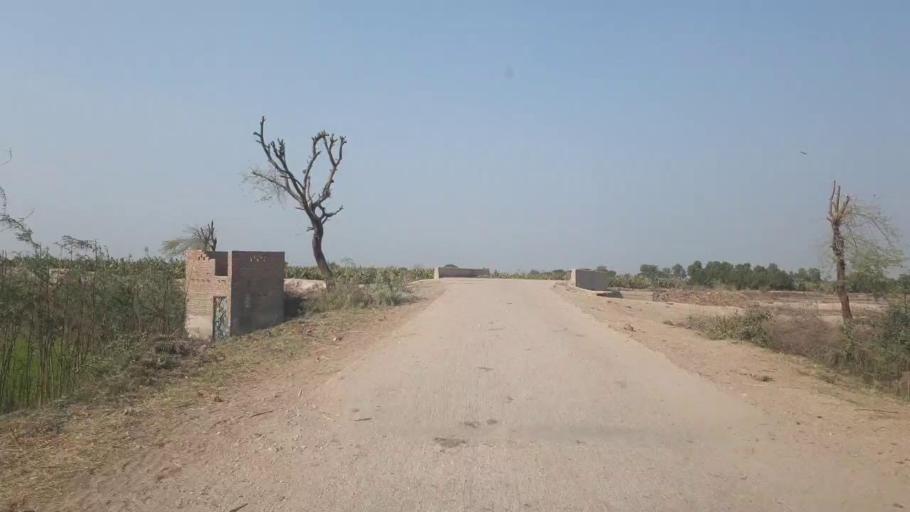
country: PK
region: Sindh
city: Tando Allahyar
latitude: 25.4445
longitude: 68.7870
